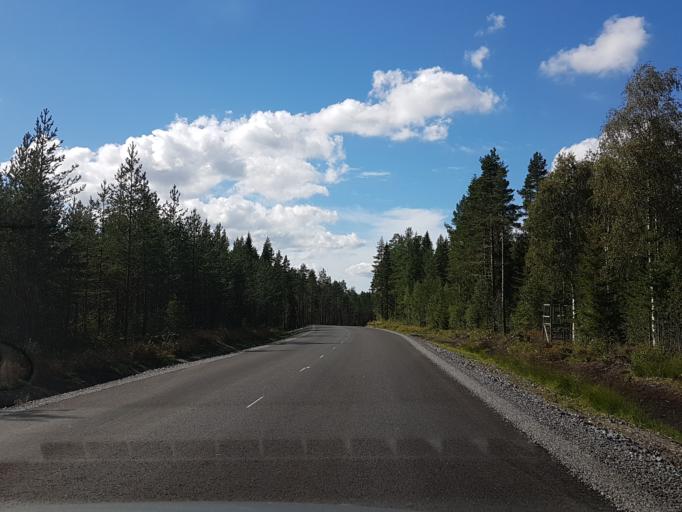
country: SE
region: Vaesterbotten
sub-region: Robertsfors Kommun
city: Robertsfors
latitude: 64.1285
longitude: 20.6530
